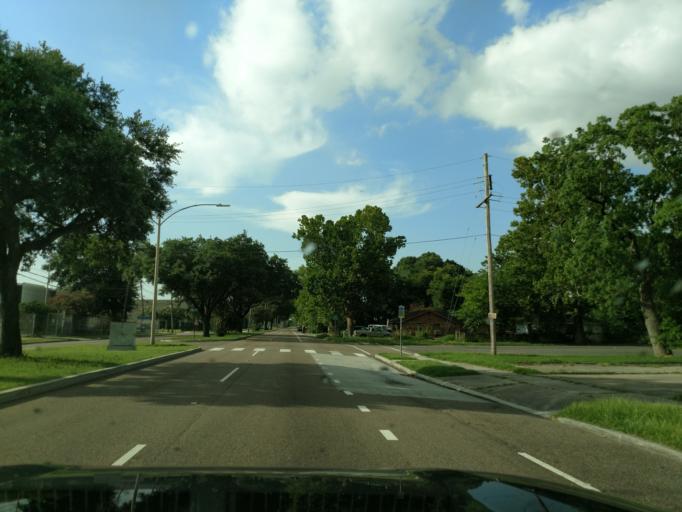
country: US
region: Louisiana
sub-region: Jefferson Parish
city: Gretna
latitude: 29.9342
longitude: -90.0415
